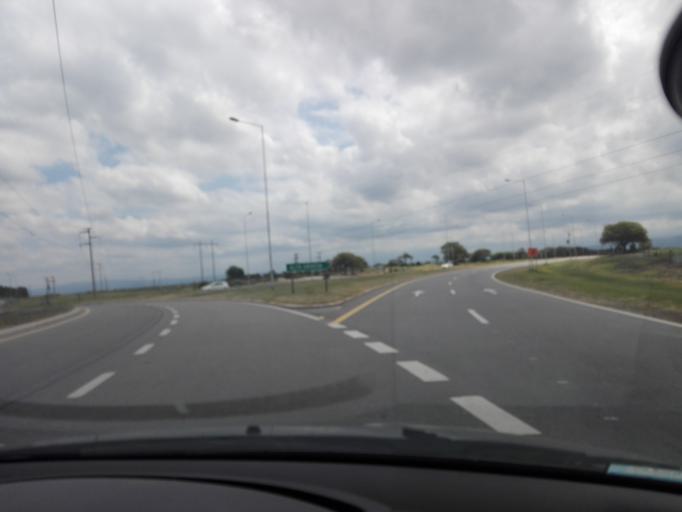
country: AR
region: Cordoba
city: Alta Gracia
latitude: -31.6517
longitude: -64.3159
